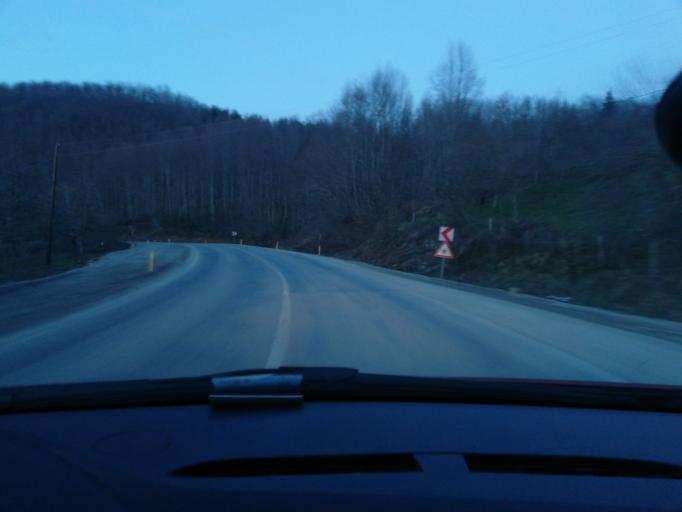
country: TR
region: Kastamonu
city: Inebolu
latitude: 41.9047
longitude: 33.7255
